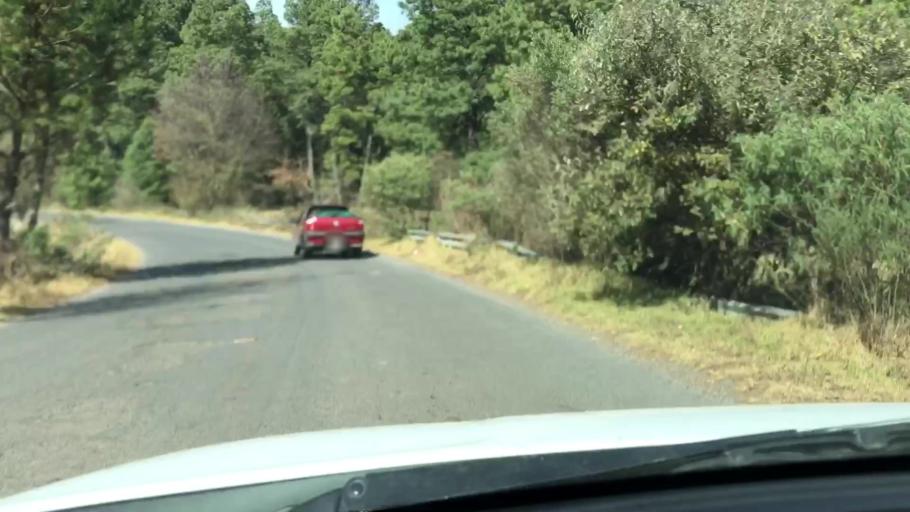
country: MX
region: Jalisco
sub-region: Amacueca
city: Tepec
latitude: 20.0517
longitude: -103.6961
